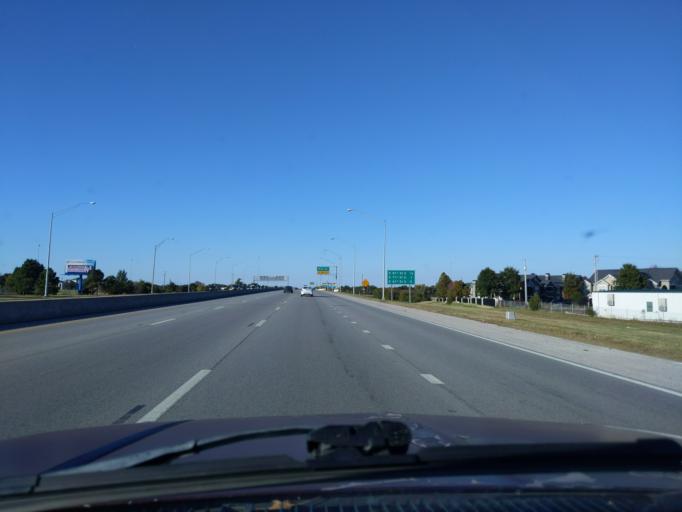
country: US
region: Oklahoma
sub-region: Tulsa County
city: Broken Arrow
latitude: 36.0425
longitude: -95.8590
